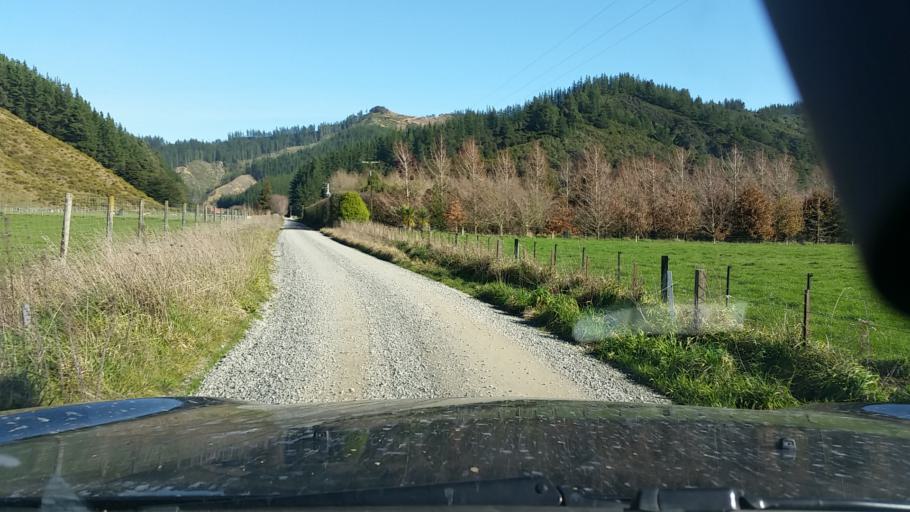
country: NZ
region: Marlborough
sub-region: Marlborough District
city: Blenheim
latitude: -41.4308
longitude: 173.7644
